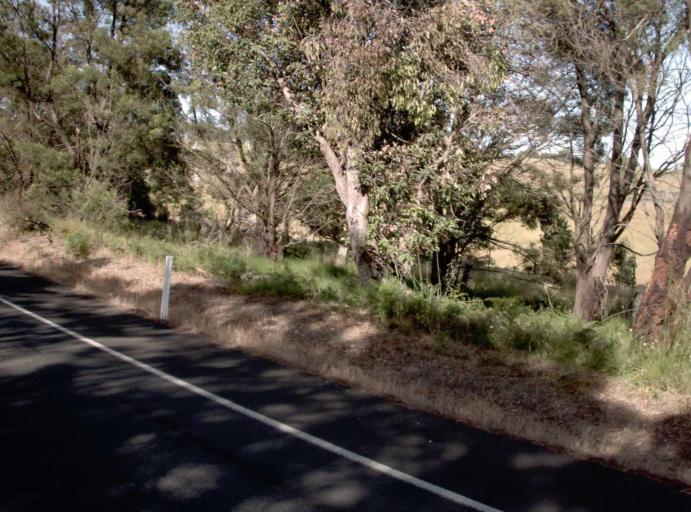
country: AU
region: Victoria
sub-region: East Gippsland
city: Lakes Entrance
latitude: -37.8498
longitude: 147.8480
